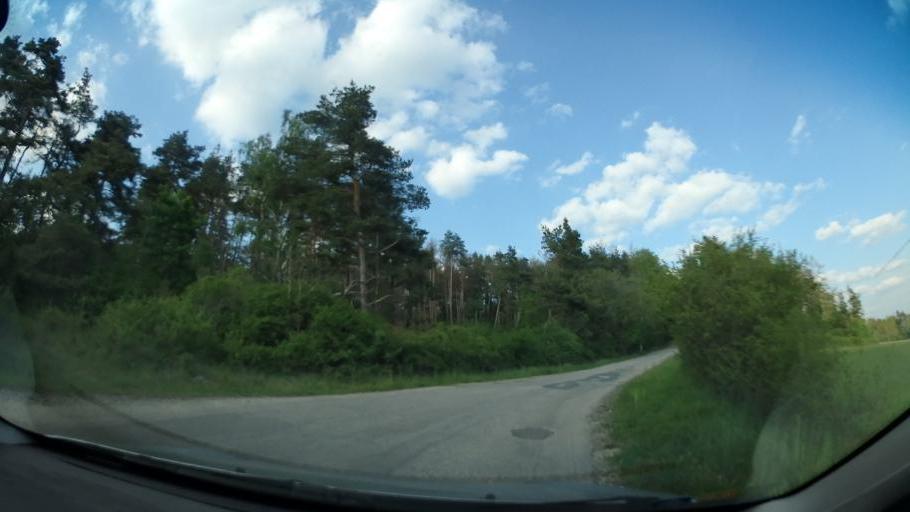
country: CZ
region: Vysocina
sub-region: Okres Zd'ar nad Sazavou
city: Velke Mezirici
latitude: 49.3445
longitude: 15.9566
